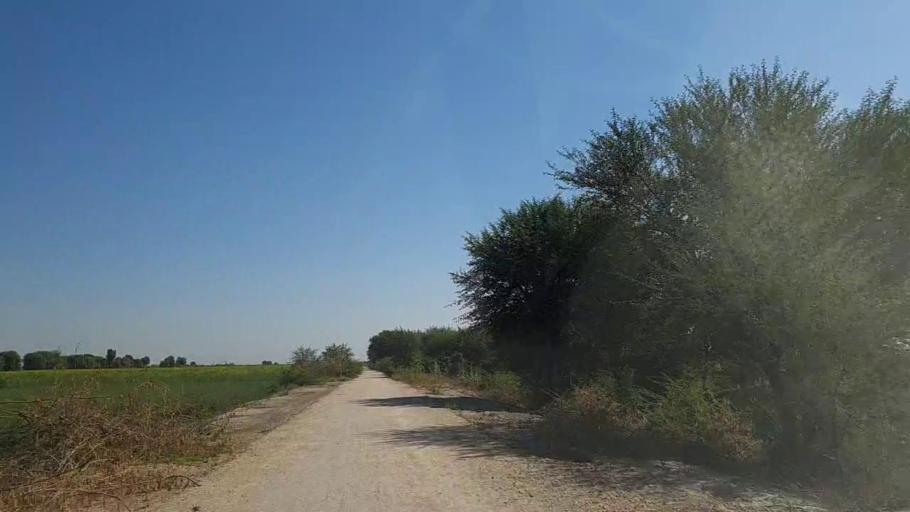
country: PK
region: Sindh
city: Dhoro Naro
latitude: 25.3526
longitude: 69.5347
